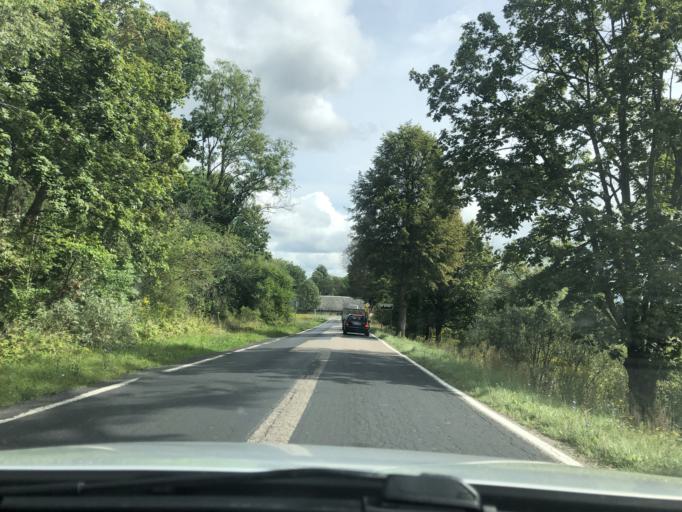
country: PL
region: Greater Poland Voivodeship
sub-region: Powiat czarnkowsko-trzcianecki
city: Wielen
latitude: 52.9057
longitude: 16.1759
